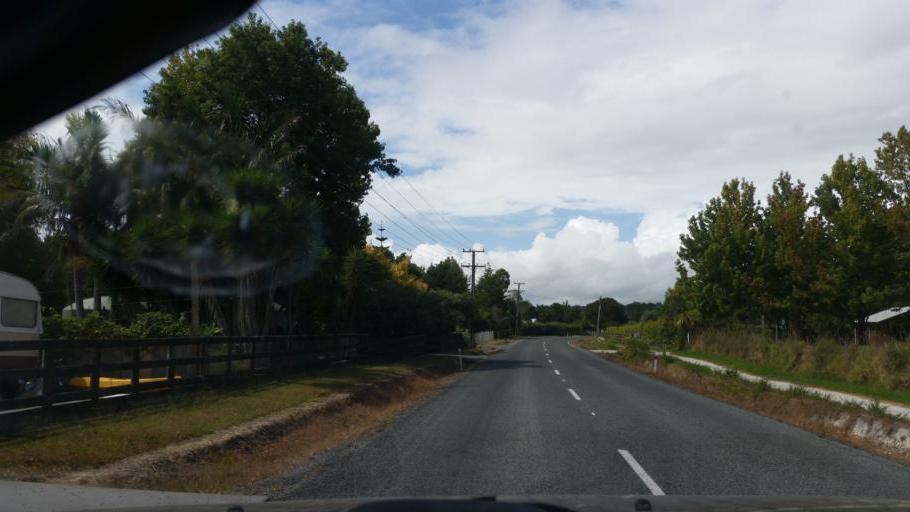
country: NZ
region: Auckland
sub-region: Auckland
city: Wellsford
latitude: -36.1242
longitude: 174.5580
